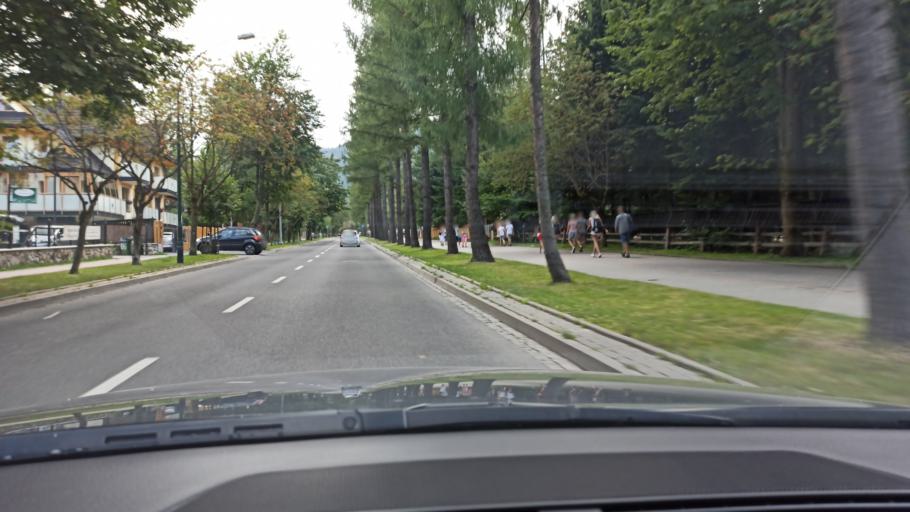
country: PL
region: Lesser Poland Voivodeship
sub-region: Powiat tatrzanski
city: Zakopane
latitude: 49.2874
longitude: 19.9615
